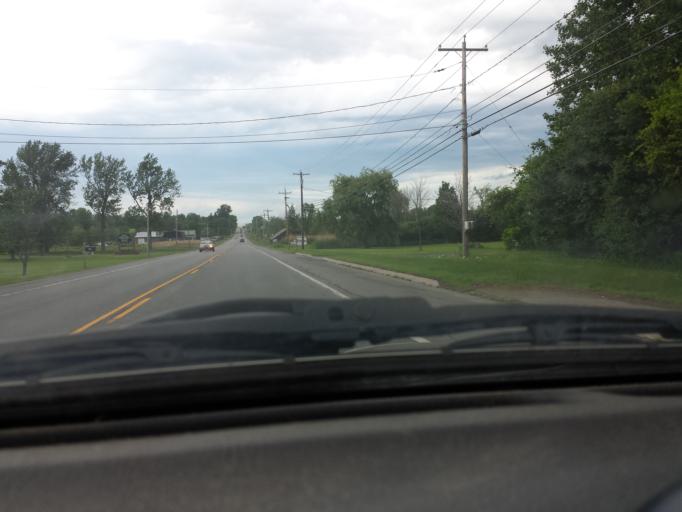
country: US
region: New York
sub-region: St. Lawrence County
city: Potsdam
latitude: 44.7000
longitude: -74.9871
